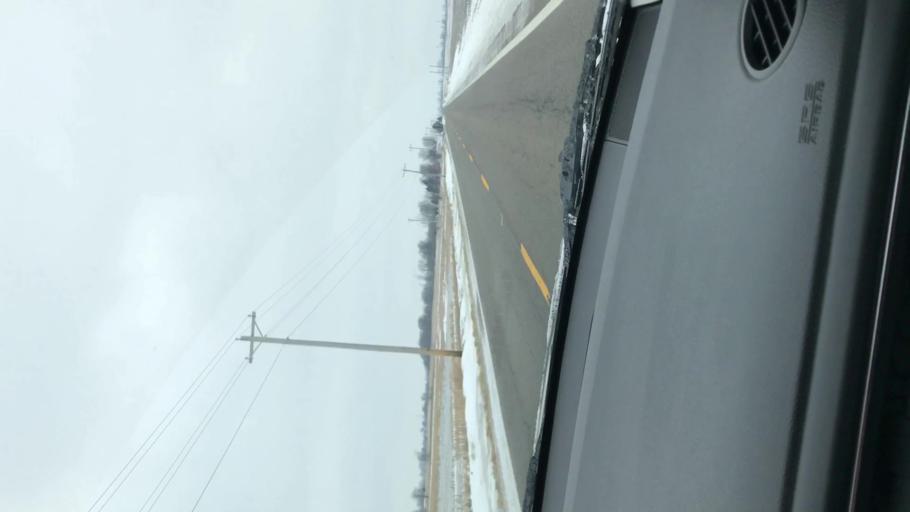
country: US
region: Ohio
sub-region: Logan County
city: Northwood
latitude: 40.4614
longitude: -83.5829
